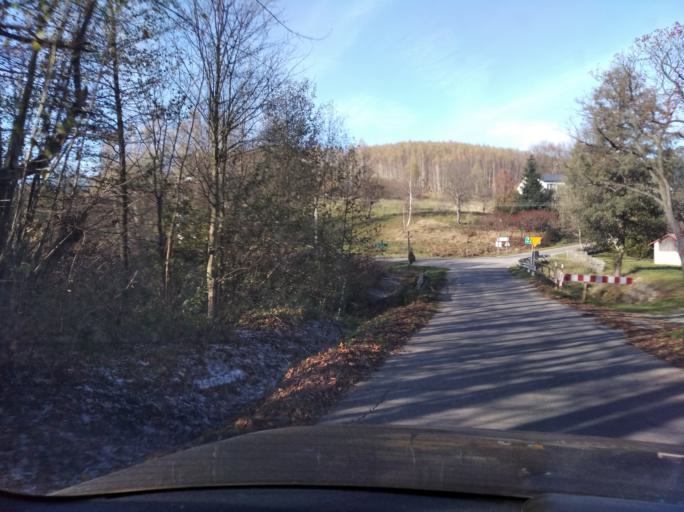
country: PL
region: Subcarpathian Voivodeship
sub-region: Powiat ropczycko-sedziszowski
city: Wielopole Skrzynskie
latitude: 49.9077
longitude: 21.5669
